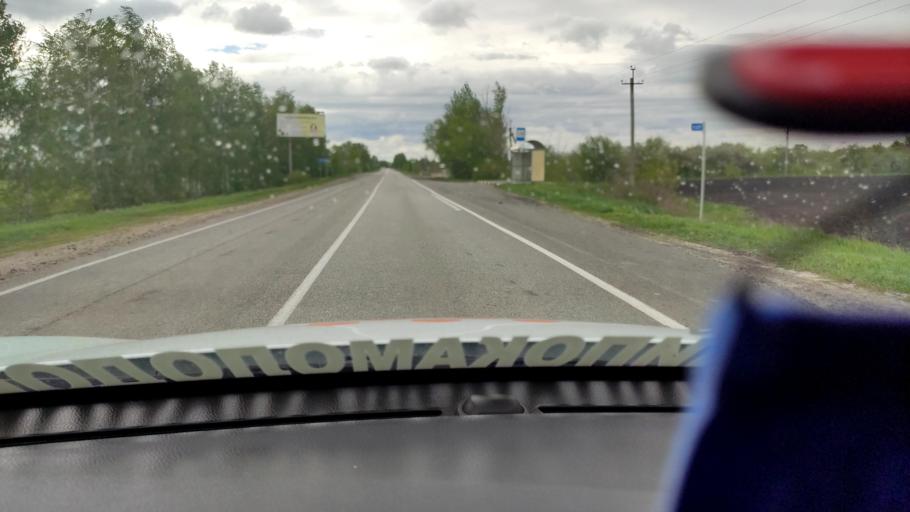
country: RU
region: Voronezj
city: Imeni Pervogo Maya
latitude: 50.7723
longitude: 39.3860
